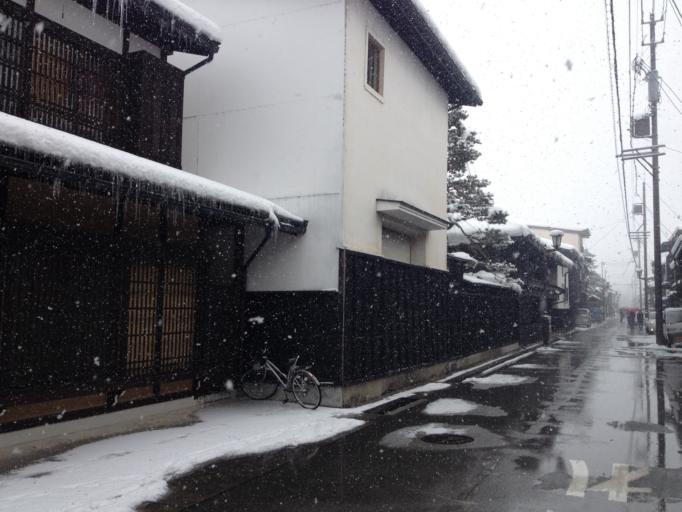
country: JP
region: Gifu
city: Takayama
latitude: 36.2351
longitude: 137.1866
